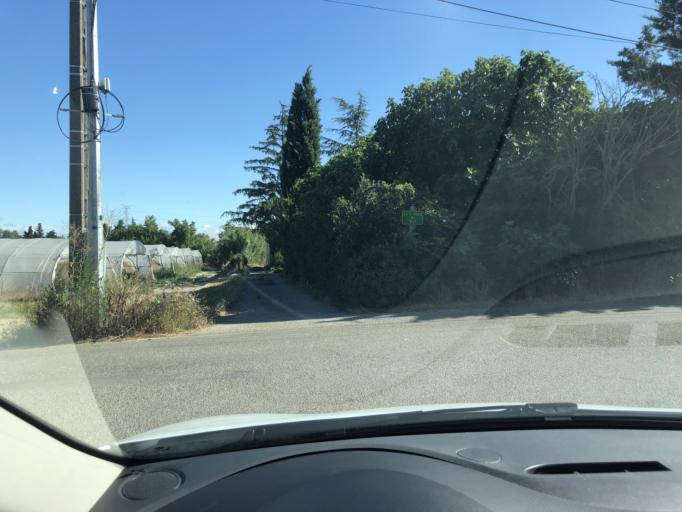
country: FR
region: Provence-Alpes-Cote d'Azur
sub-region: Departement des Bouches-du-Rhone
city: Chateaurenard
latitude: 43.8971
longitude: 4.8664
